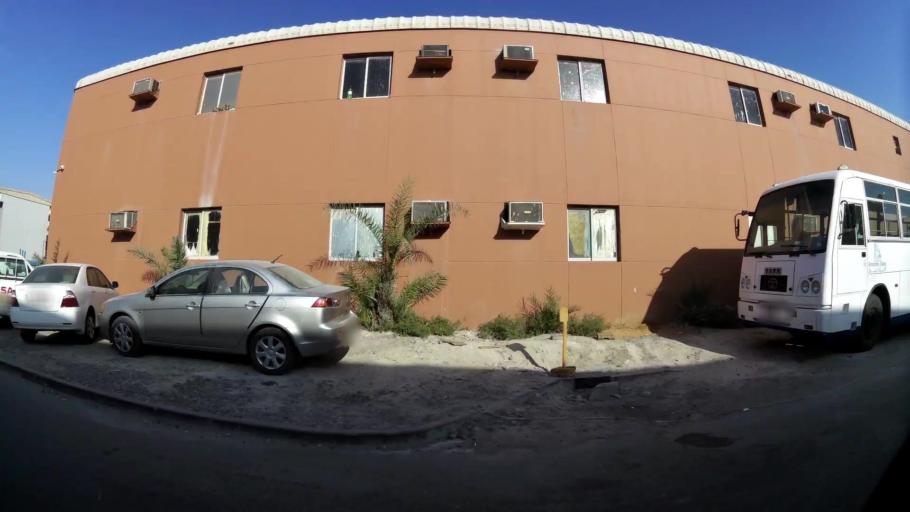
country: AE
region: Dubai
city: Dubai
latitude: 25.1317
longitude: 55.2529
